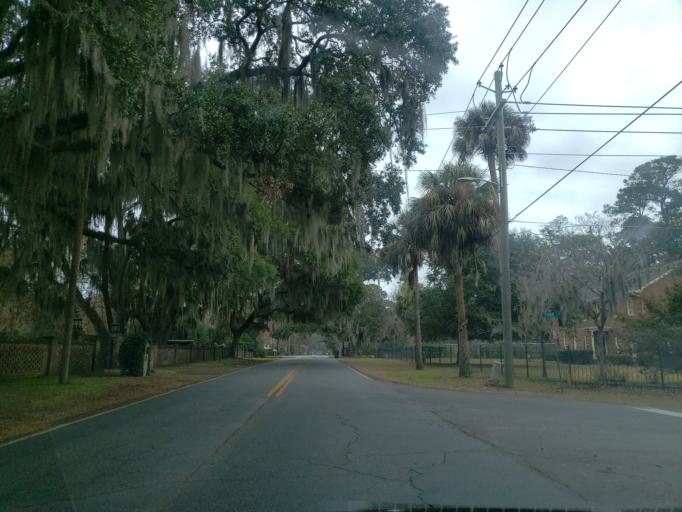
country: US
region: Georgia
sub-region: Chatham County
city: Wilmington Island
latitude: 31.9837
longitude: -80.9956
